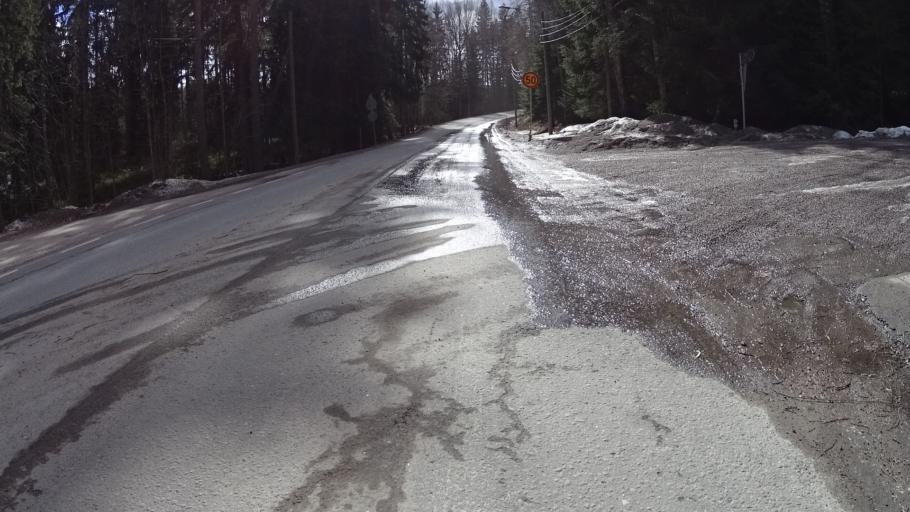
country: FI
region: Uusimaa
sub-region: Helsinki
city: Kauniainen
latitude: 60.3097
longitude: 24.7074
